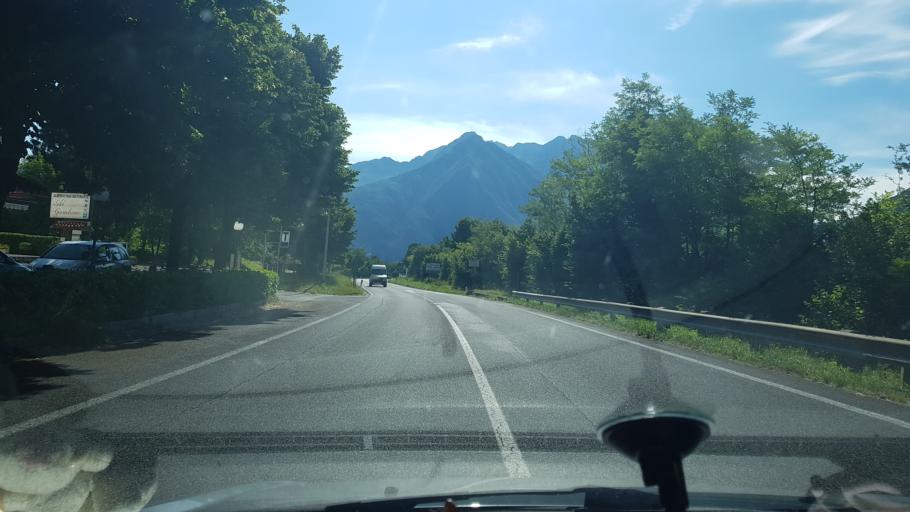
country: IT
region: Friuli Venezia Giulia
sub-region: Provincia di Udine
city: Amaro
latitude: 46.3715
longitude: 13.0842
